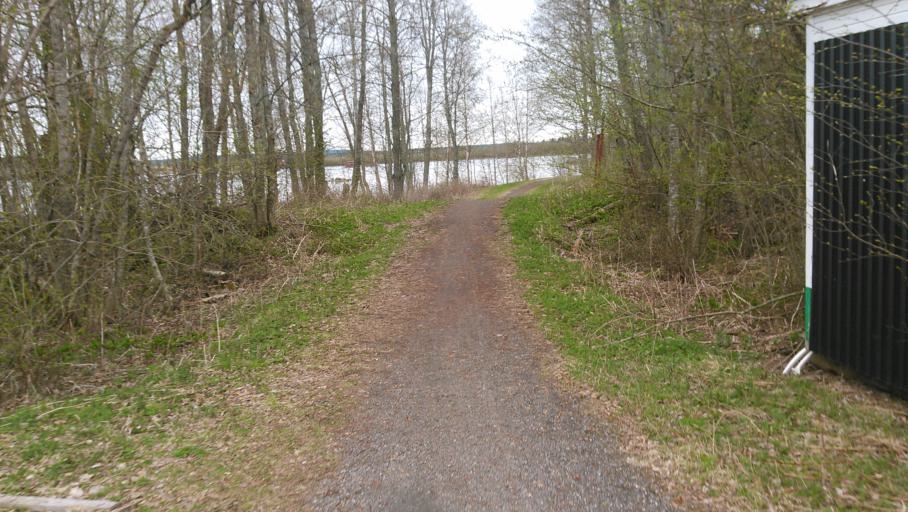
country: SE
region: Vaesterbotten
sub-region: Umea Kommun
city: Umea
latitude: 63.7800
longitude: 20.3193
